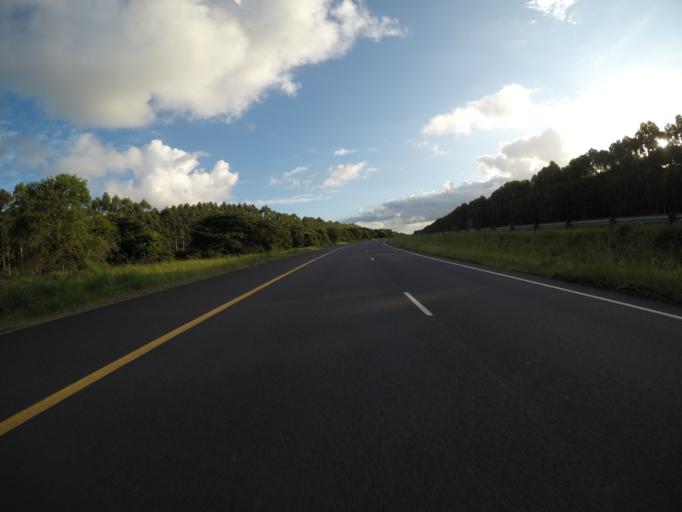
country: ZA
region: KwaZulu-Natal
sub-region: uThungulu District Municipality
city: KwaMbonambi
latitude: -28.5274
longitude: 32.1378
